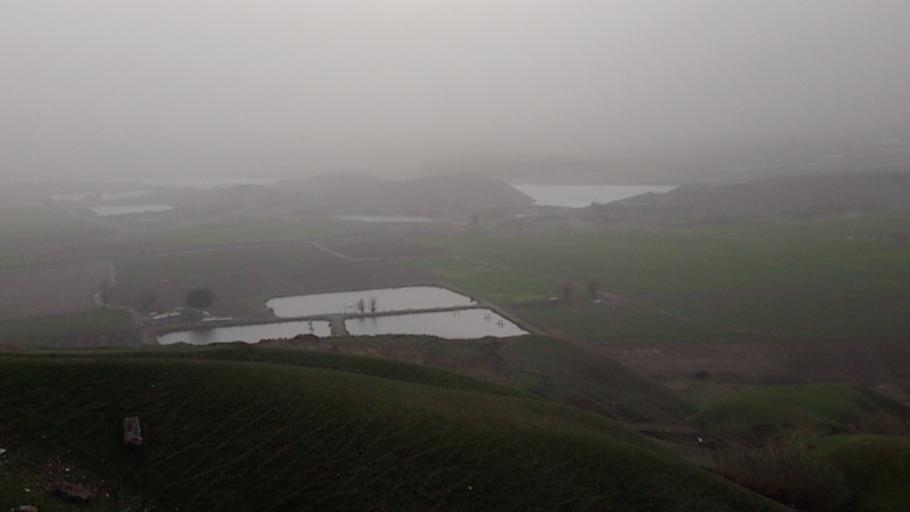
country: IQ
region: As Sulaymaniyah
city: Qeladize
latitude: 36.1563
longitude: 45.1235
